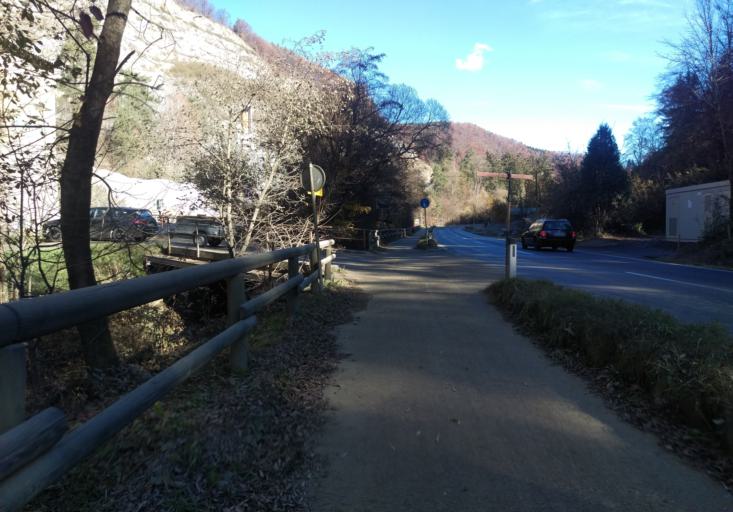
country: AT
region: Styria
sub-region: Politischer Bezirk Graz-Umgebung
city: Stattegg
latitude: 47.1315
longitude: 15.4501
